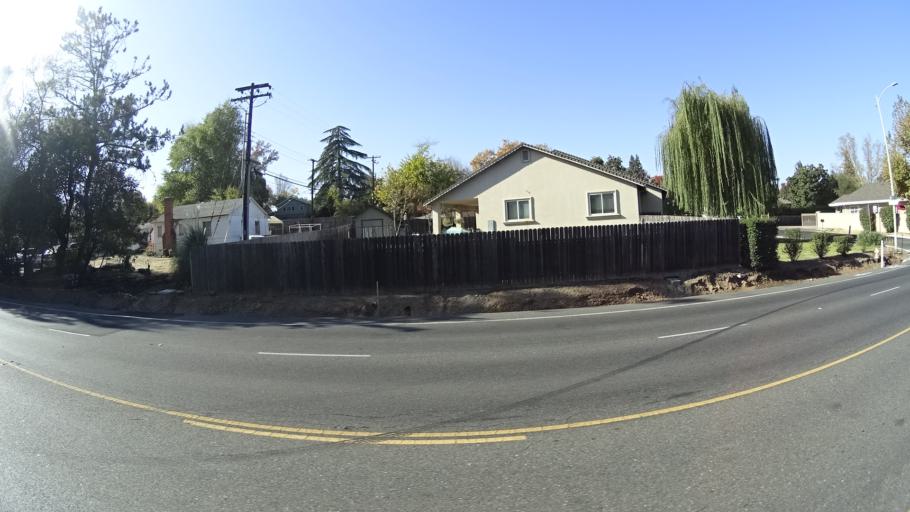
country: US
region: California
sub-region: Sacramento County
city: Fair Oaks
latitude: 38.6579
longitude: -121.2921
